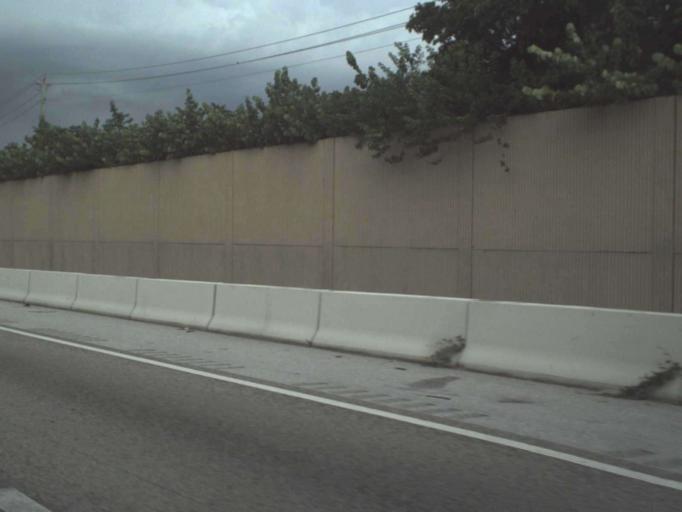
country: US
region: Florida
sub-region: Palm Beach County
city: West Palm Beach
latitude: 26.7131
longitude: -80.0820
